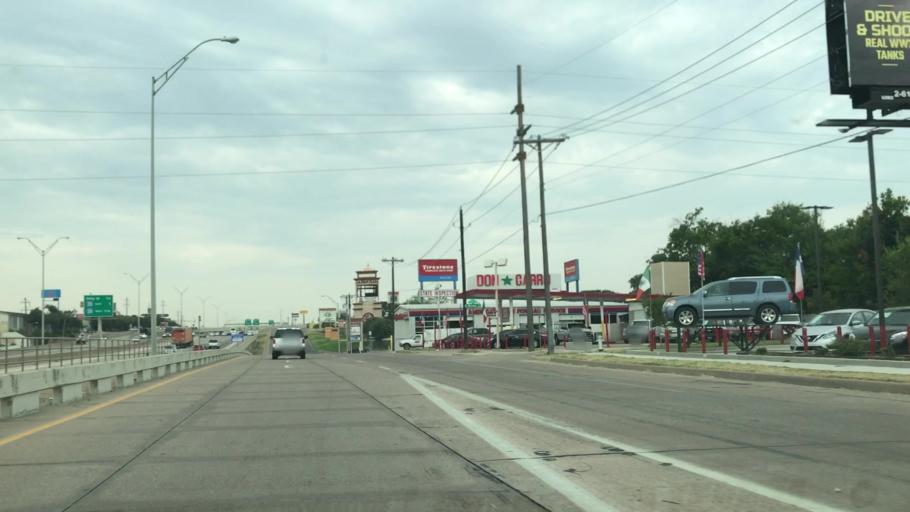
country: US
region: Texas
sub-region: Tarrant County
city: Fort Worth
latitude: 32.6897
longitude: -97.3210
